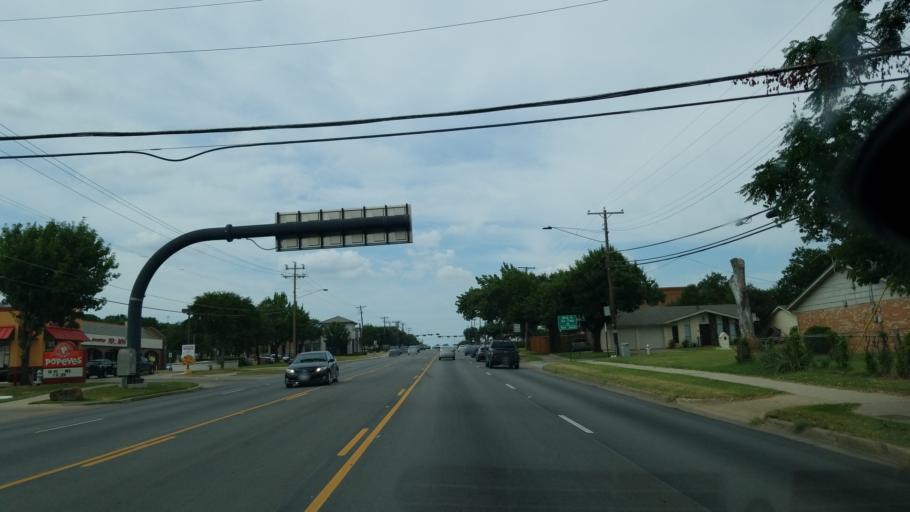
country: US
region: Texas
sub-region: Tarrant County
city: Arlington
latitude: 32.7526
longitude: -97.0973
